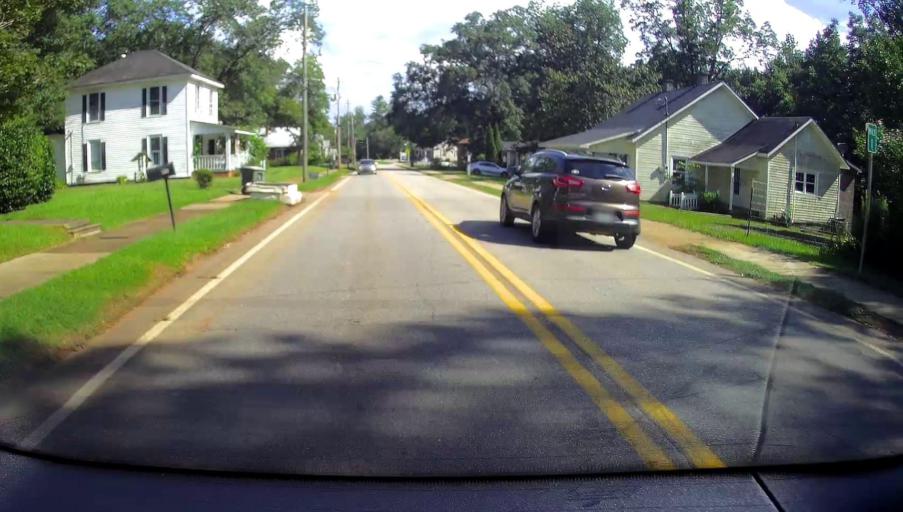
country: US
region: Georgia
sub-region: Upson County
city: Thomaston
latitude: 32.8915
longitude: -84.3343
